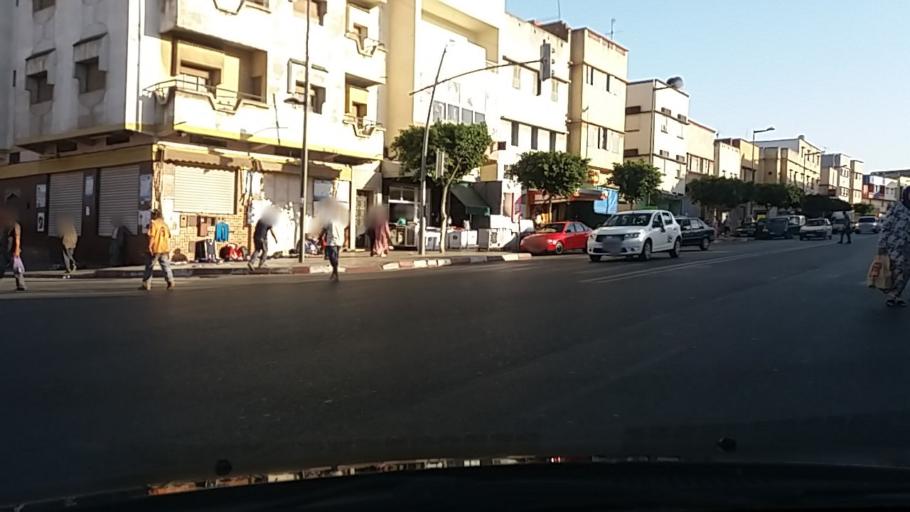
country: MA
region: Gharb-Chrarda-Beni Hssen
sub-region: Kenitra Province
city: Kenitra
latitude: 34.2675
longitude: -6.5624
